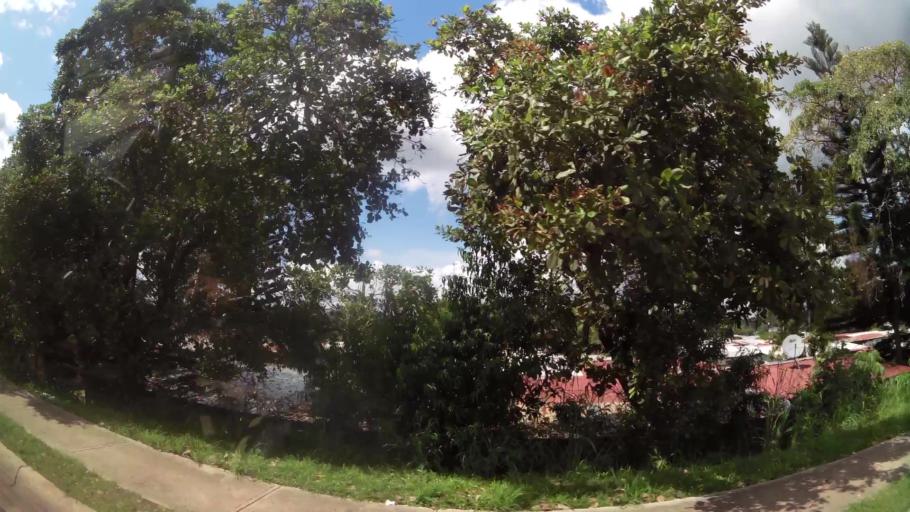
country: PA
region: Panama
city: Nuevo Arraijan
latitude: 8.9211
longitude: -79.7074
